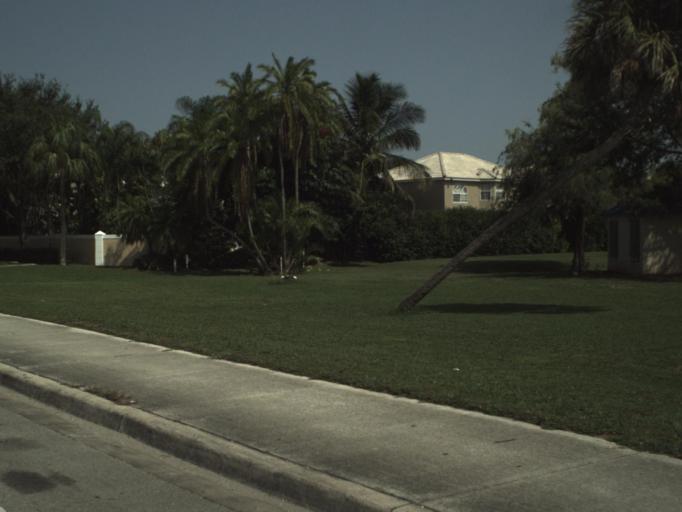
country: US
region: Florida
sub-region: Broward County
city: Margate
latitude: 26.2720
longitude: -80.2289
